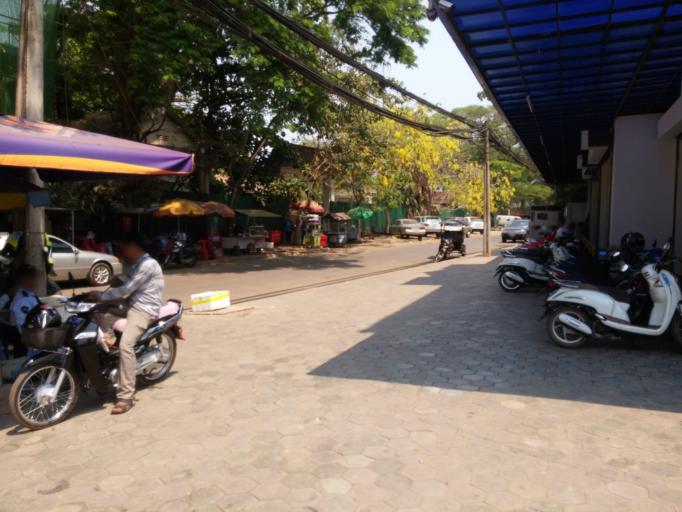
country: KH
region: Siem Reap
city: Siem Reap
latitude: 13.3578
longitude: 103.8575
